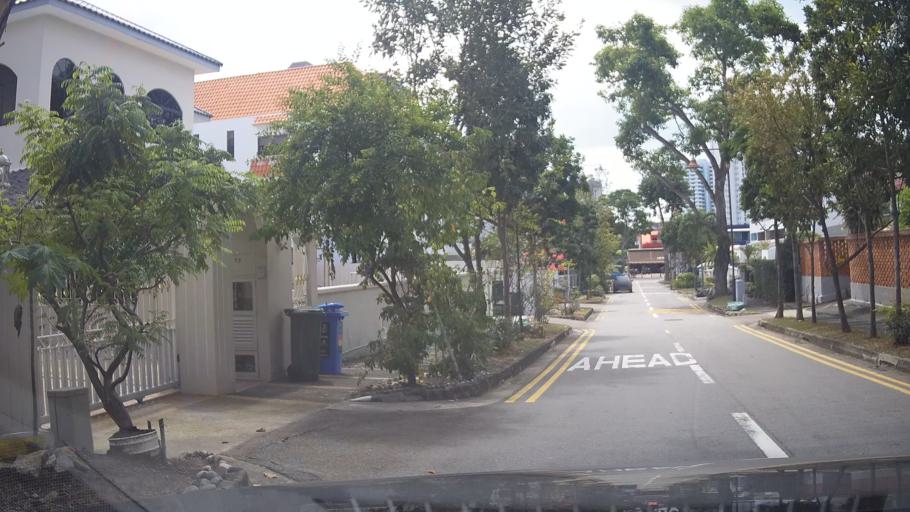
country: SG
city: Singapore
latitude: 1.3138
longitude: 103.9252
